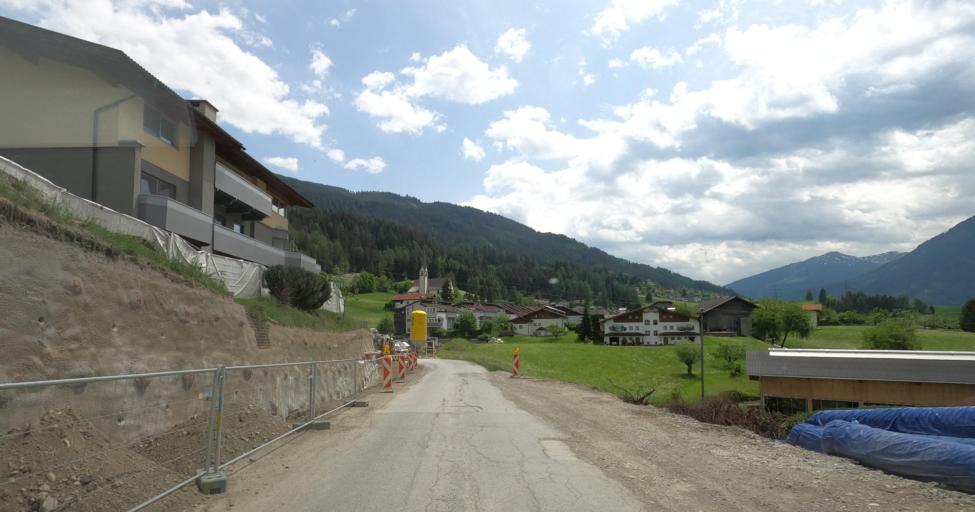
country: AT
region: Tyrol
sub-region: Politischer Bezirk Innsbruck Land
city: Pfons
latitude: 47.1438
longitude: 11.4592
